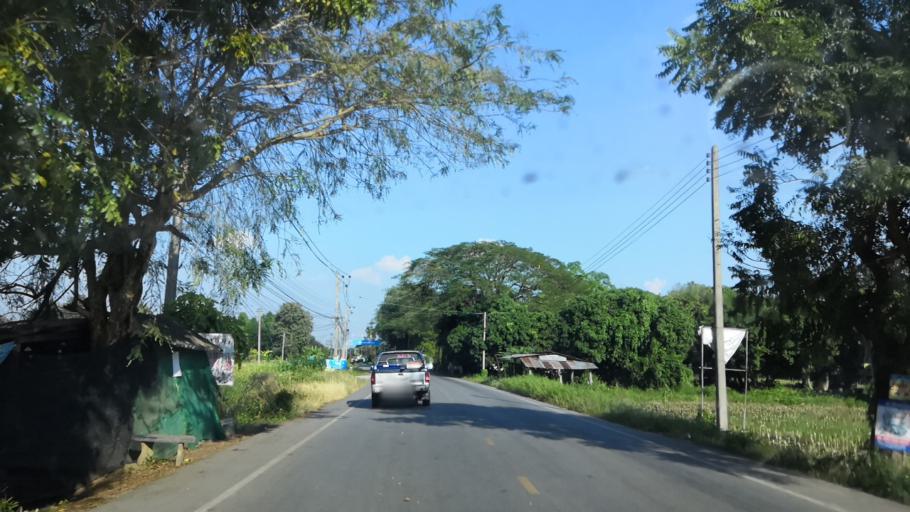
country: TH
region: Chiang Rai
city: Wiang Chai
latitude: 19.9327
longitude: 99.8992
